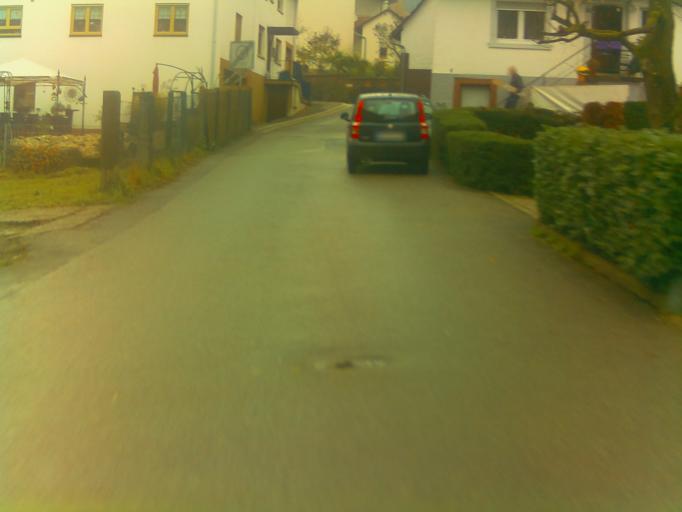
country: DE
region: Baden-Wuerttemberg
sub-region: Karlsruhe Region
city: Schonau
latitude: 49.4548
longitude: 8.8071
